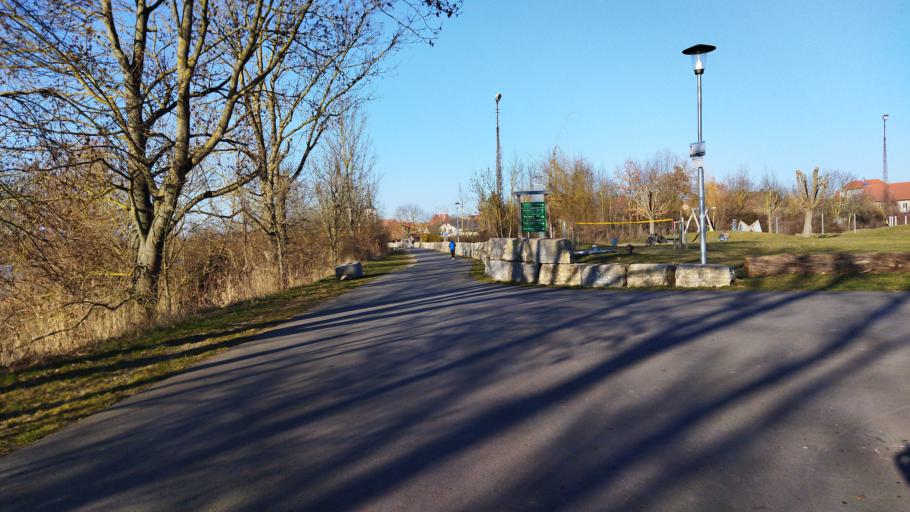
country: DE
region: Bavaria
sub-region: Regierungsbezirk Unterfranken
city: Albertshofen
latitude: 49.7673
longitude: 10.1574
